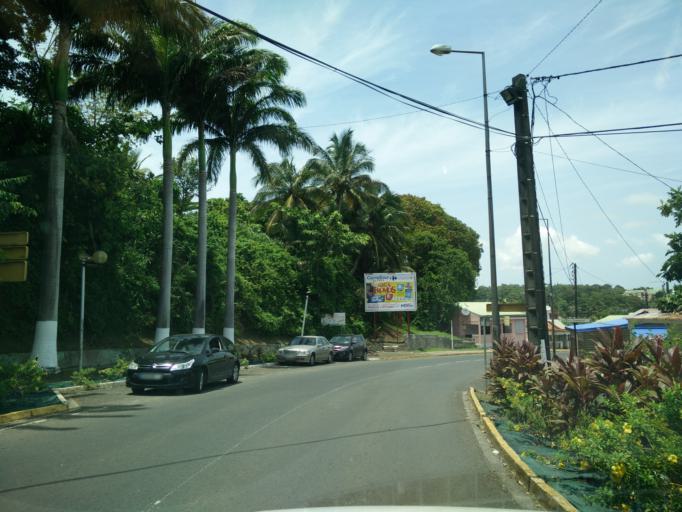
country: GP
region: Guadeloupe
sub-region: Guadeloupe
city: Petit-Bourg
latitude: 16.1891
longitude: -61.5908
